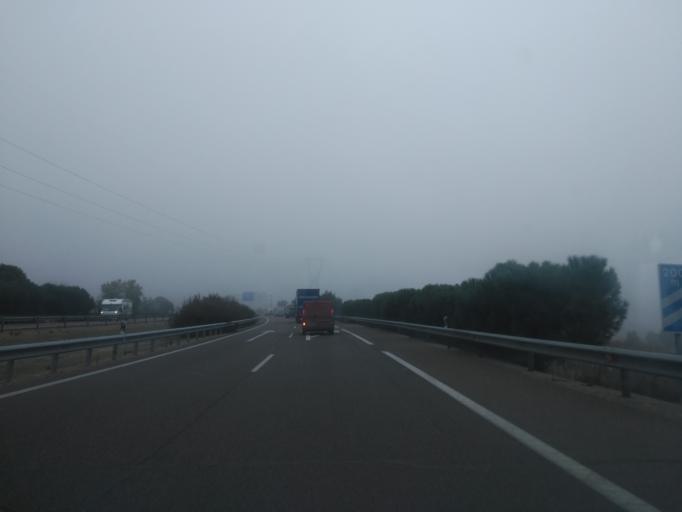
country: ES
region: Castille and Leon
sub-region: Provincia de Valladolid
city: Arroyo
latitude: 41.6301
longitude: -4.7791
